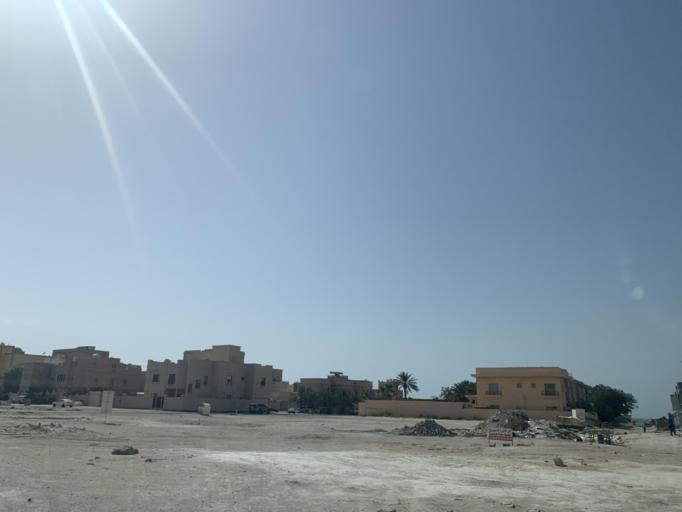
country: BH
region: Manama
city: Jidd Hafs
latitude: 26.2325
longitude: 50.4852
